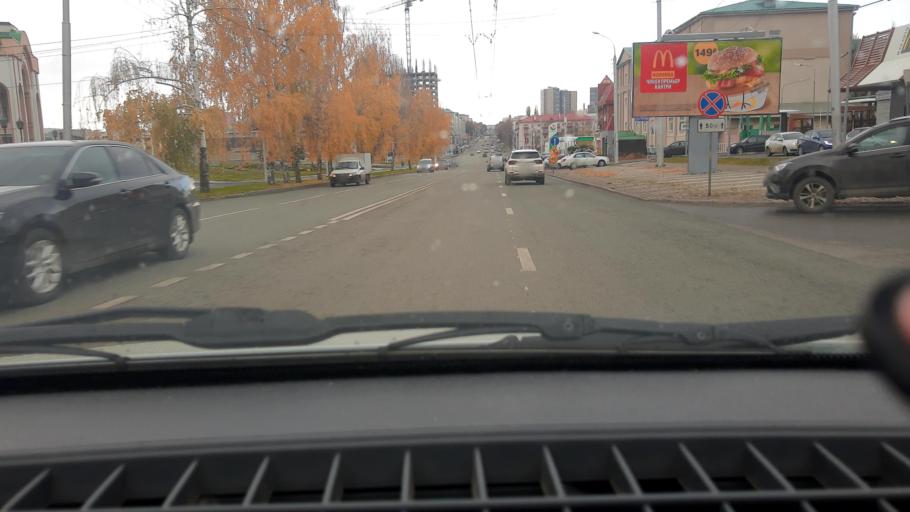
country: RU
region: Bashkortostan
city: Ufa
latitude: 54.7487
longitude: 56.0216
